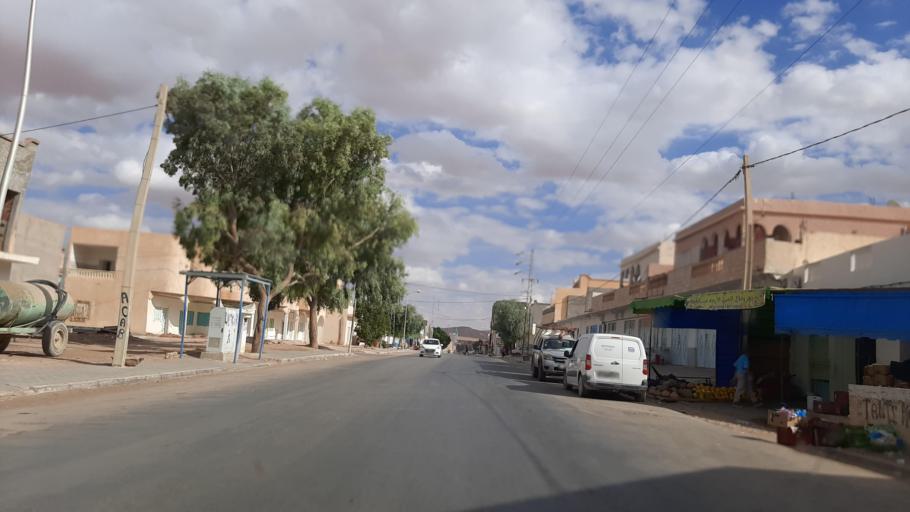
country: TN
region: Tataouine
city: Tataouine
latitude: 32.9226
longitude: 10.4595
